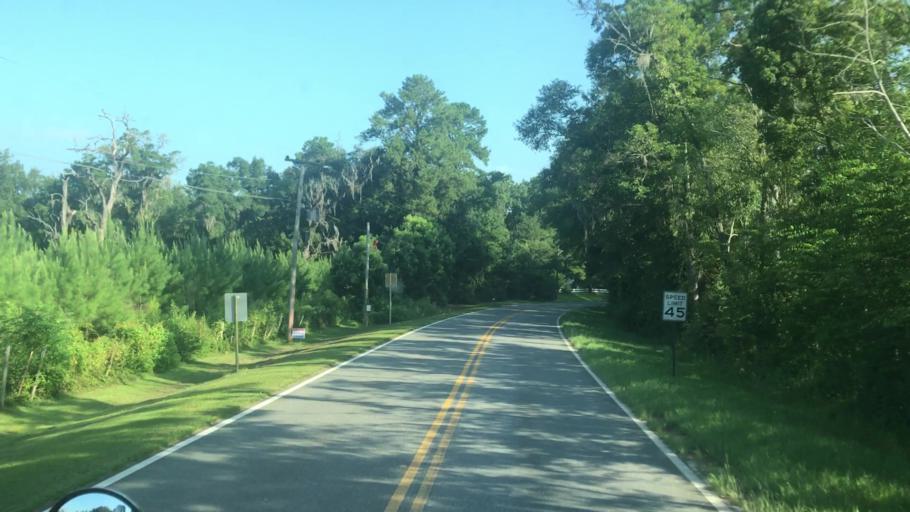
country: US
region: Florida
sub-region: Gadsden County
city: Quincy
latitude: 30.6073
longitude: -84.5732
